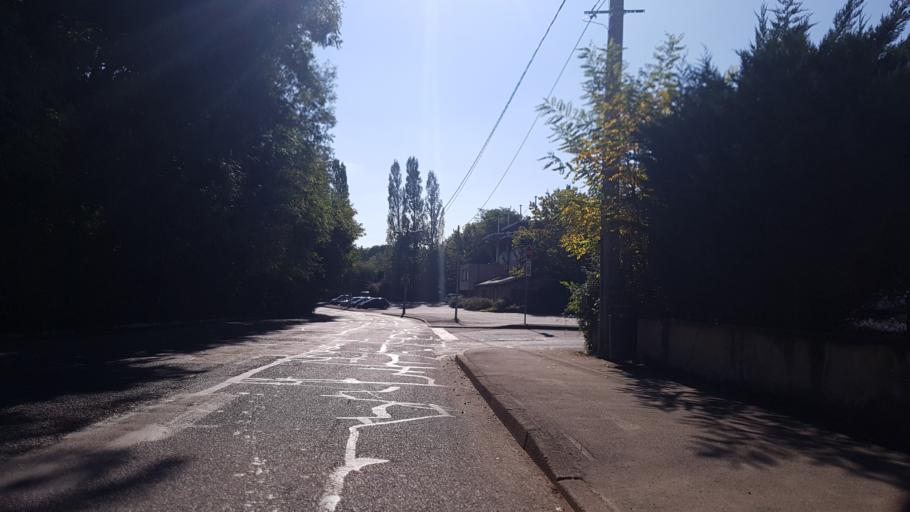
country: FR
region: Rhone-Alpes
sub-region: Departement du Rhone
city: Ecully
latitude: 45.7996
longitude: 4.7794
